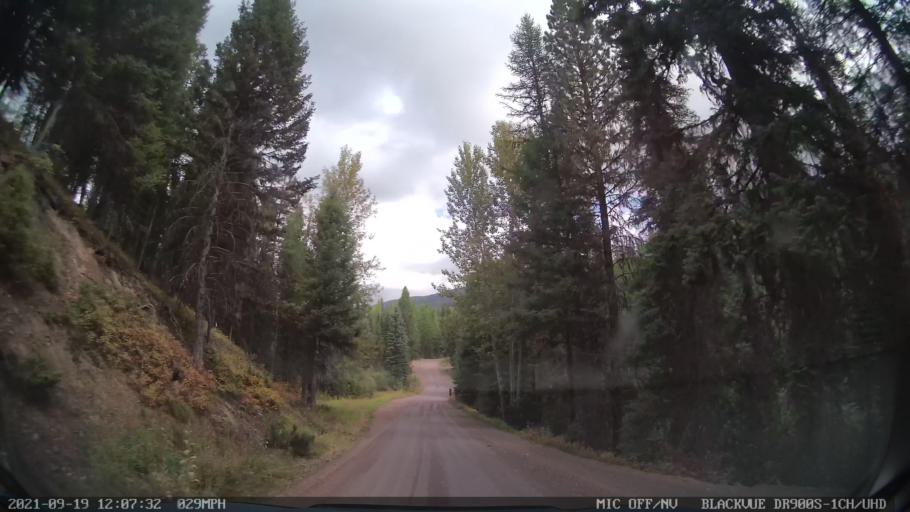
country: US
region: Montana
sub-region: Missoula County
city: Seeley Lake
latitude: 47.1843
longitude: -113.4060
